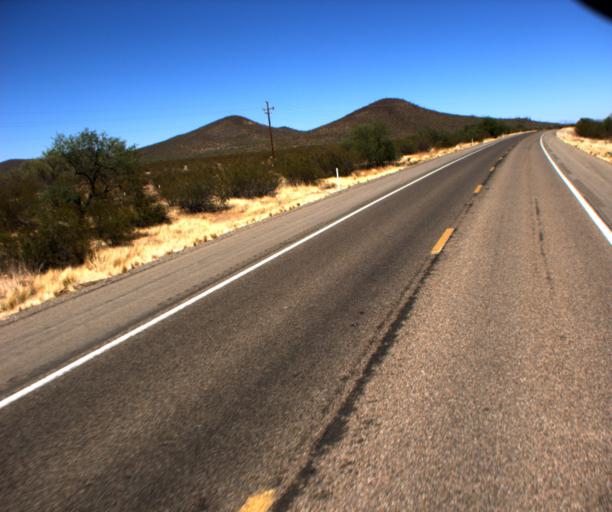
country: US
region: Arizona
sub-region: Pima County
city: Three Points
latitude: 32.0598
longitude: -111.3966
